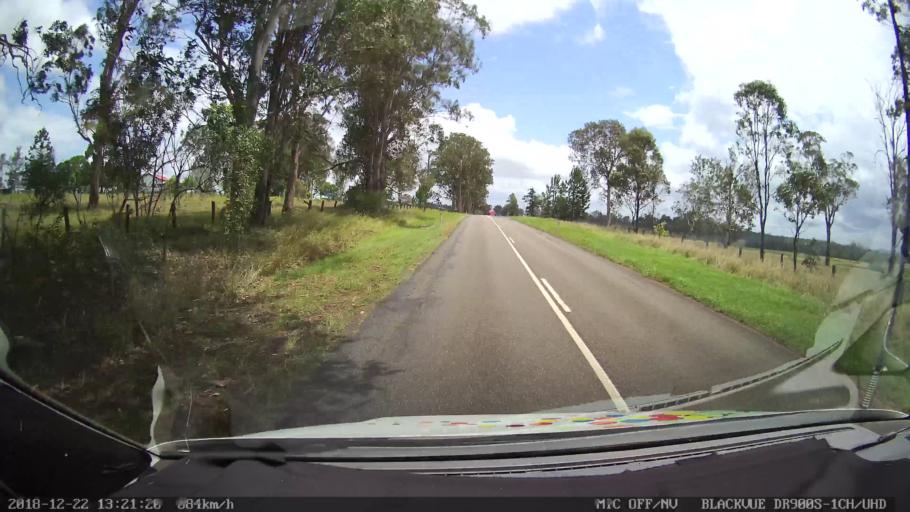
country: AU
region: New South Wales
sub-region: Clarence Valley
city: Coutts Crossing
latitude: -29.7759
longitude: 152.9213
